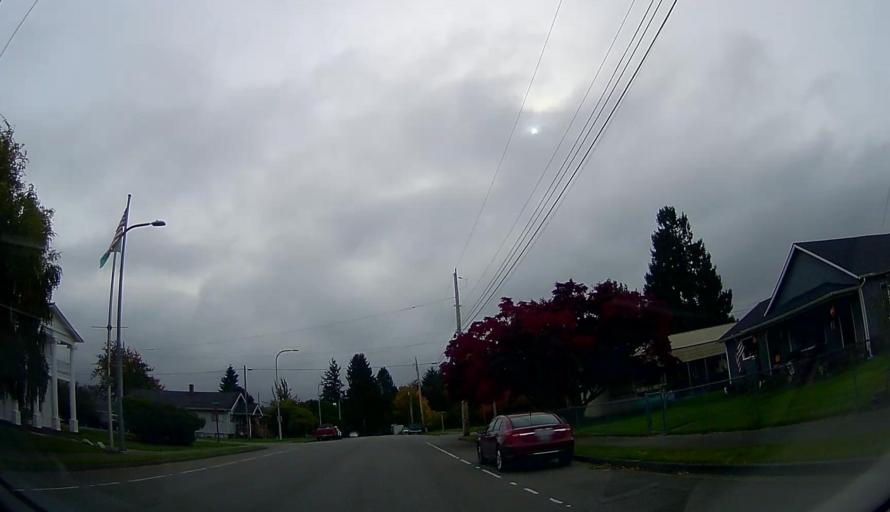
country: US
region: Washington
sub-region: Skagit County
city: Sedro-Woolley
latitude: 48.5249
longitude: -122.0598
